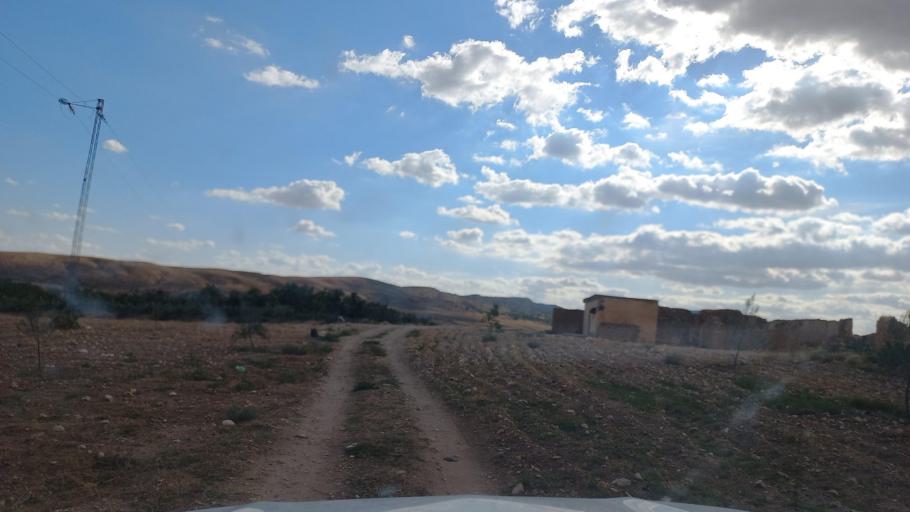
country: TN
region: Al Qasrayn
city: Sbiba
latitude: 35.4008
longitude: 9.0165
